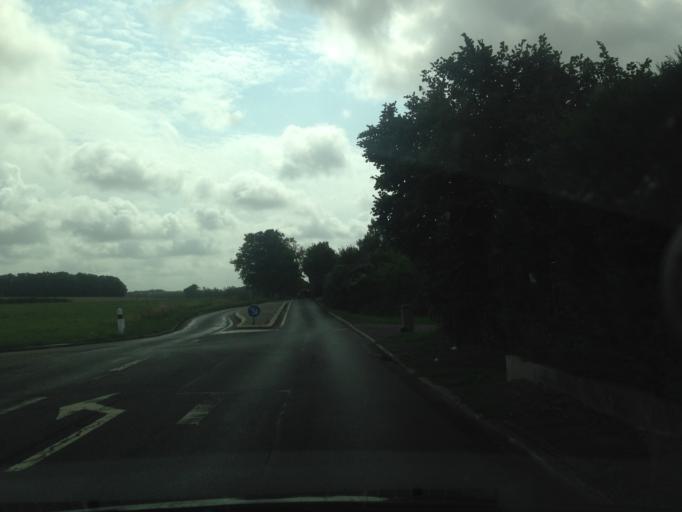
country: FR
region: Ile-de-France
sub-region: Departement du Val-d'Oise
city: Osny
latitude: 49.1206
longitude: 2.0506
